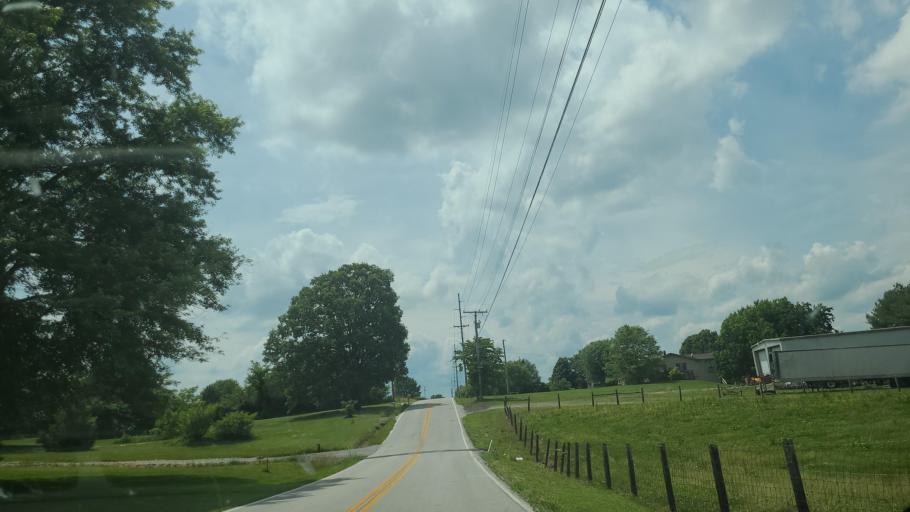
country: US
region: Tennessee
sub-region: Cumberland County
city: Crossville
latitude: 35.9063
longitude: -85.0068
